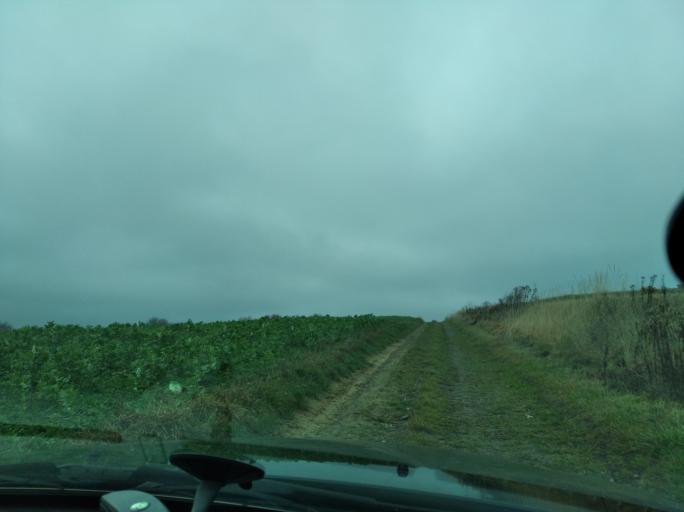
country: PL
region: Subcarpathian Voivodeship
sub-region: Powiat przeworski
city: Jawornik Polski
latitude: 49.8917
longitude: 22.2770
